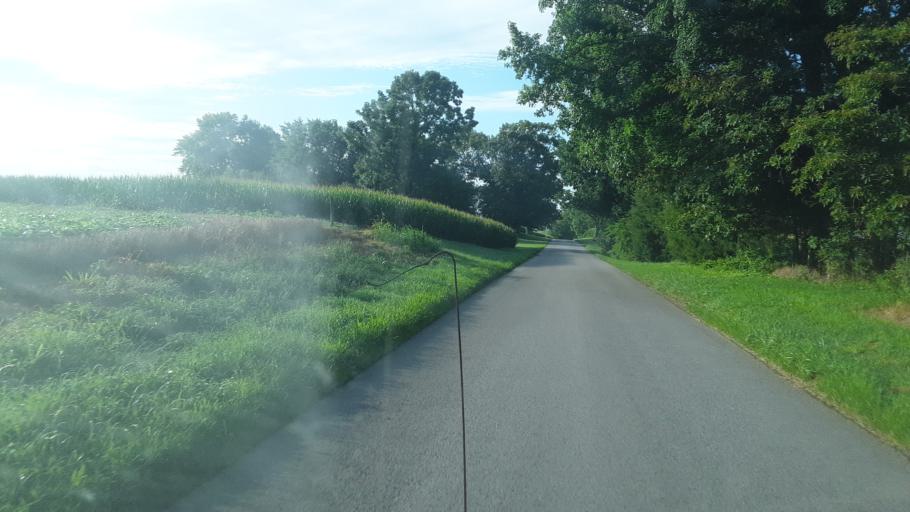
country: US
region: Kentucky
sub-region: Todd County
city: Guthrie
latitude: 36.6850
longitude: -87.1702
